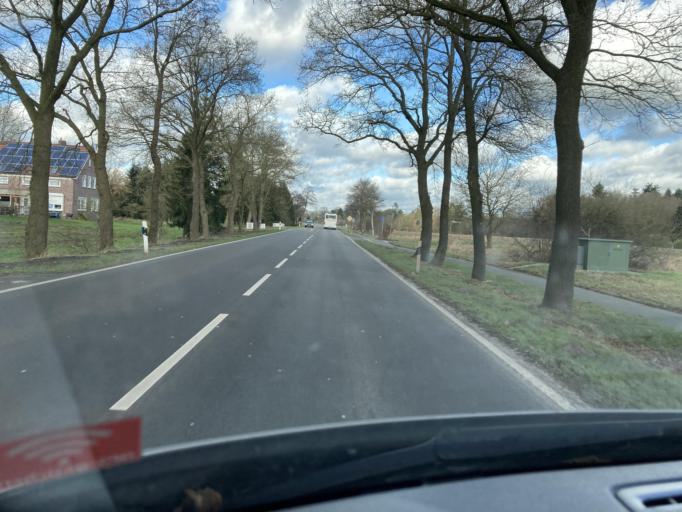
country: DE
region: Lower Saxony
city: Ostrhauderfehn
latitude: 53.1501
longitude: 7.5629
